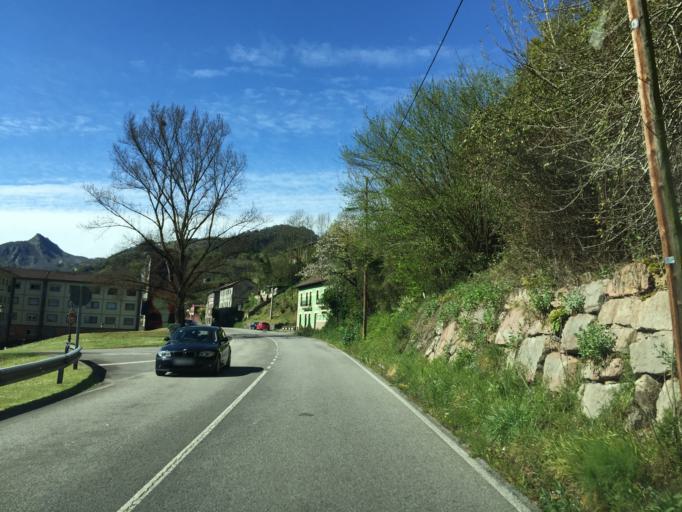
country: ES
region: Asturias
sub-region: Province of Asturias
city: Proaza
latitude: 43.3409
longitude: -5.9836
